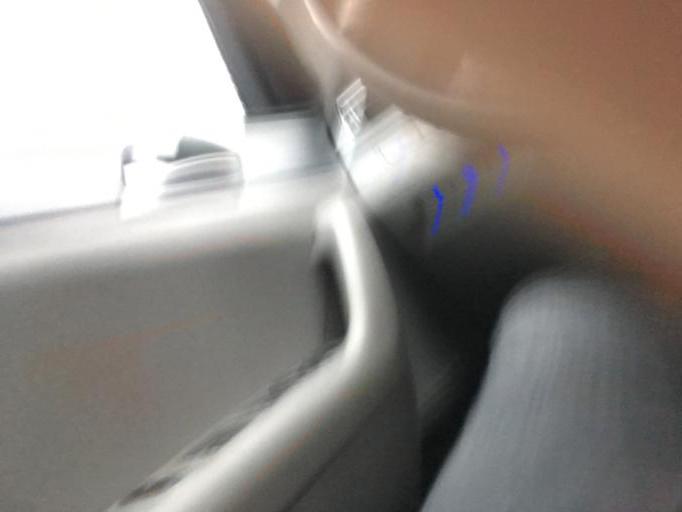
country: US
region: Michigan
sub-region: Macomb County
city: Clinton
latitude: 42.6262
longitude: -82.9442
